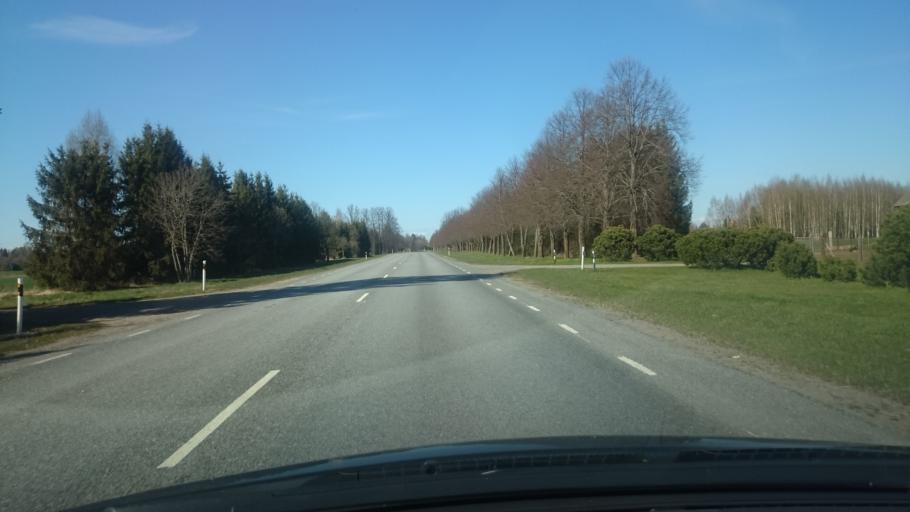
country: EE
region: Polvamaa
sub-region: Polva linn
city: Polva
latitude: 58.2550
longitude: 27.0022
